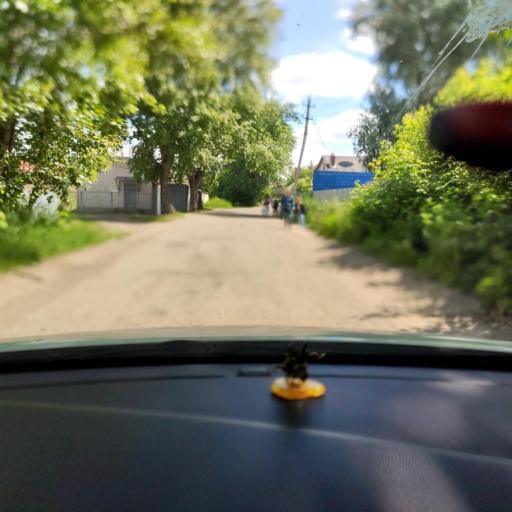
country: RU
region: Tatarstan
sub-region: Zelenodol'skiy Rayon
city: Vasil'yevo
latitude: 55.8375
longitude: 48.7070
